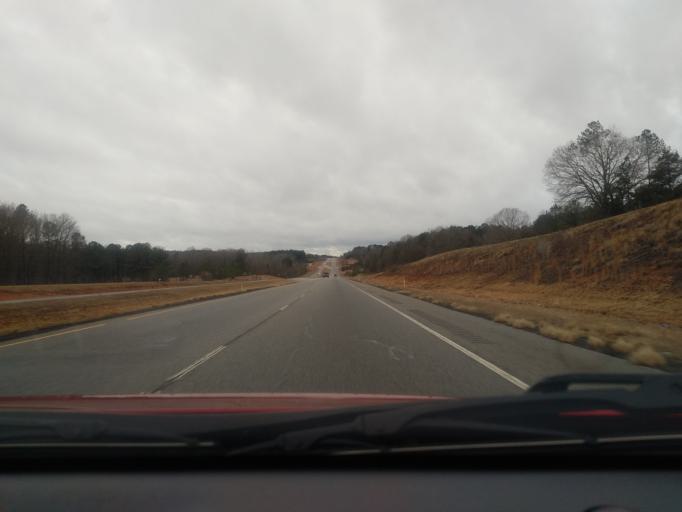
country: US
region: Georgia
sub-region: Spalding County
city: East Griffin
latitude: 33.2549
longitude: -84.1408
